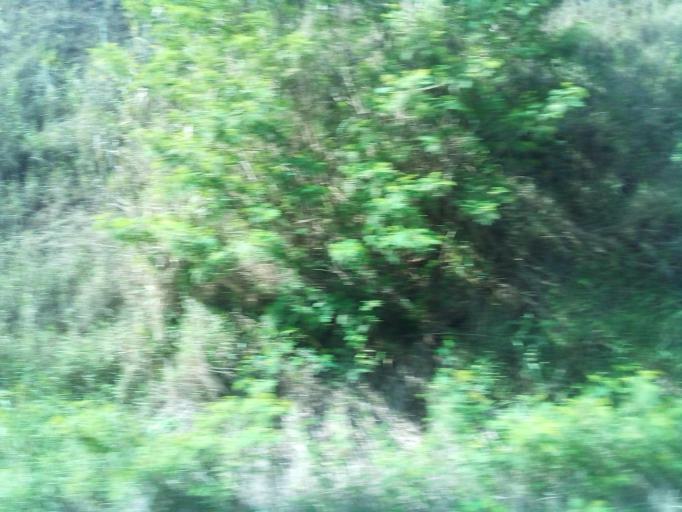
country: BR
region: Minas Gerais
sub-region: Raposos
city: Raposos
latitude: -19.8724
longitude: -43.7705
